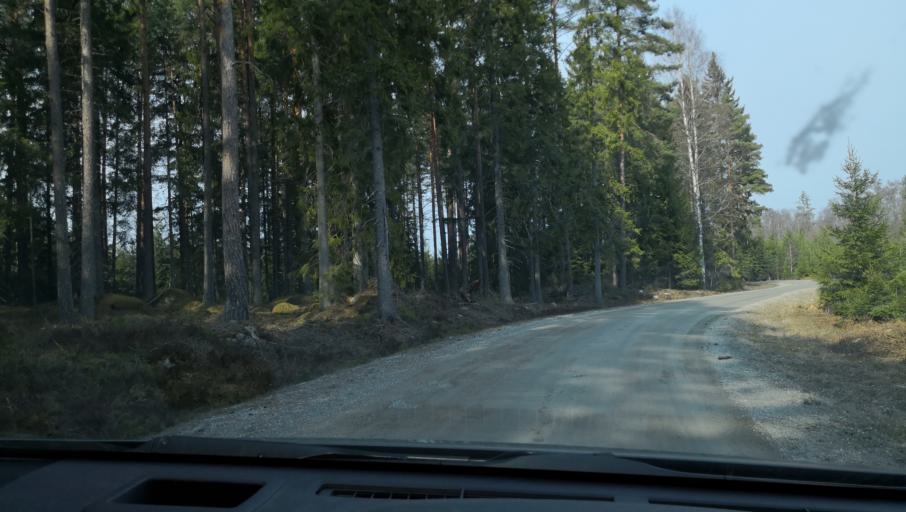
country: SE
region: OErebro
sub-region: Lindesbergs Kommun
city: Frovi
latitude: 59.3614
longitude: 15.4325
